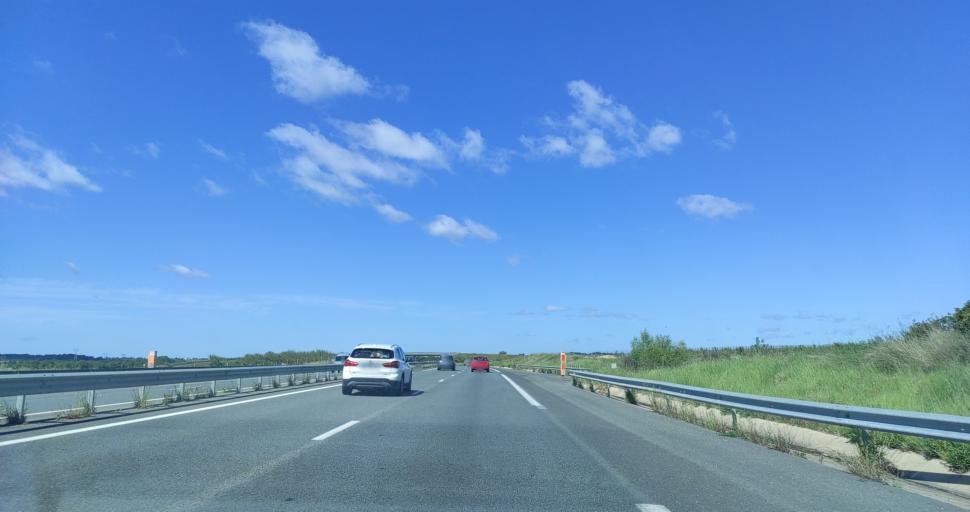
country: FR
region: Languedoc-Roussillon
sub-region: Departement de l'Herault
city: Valros
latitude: 43.4108
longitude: 3.3658
